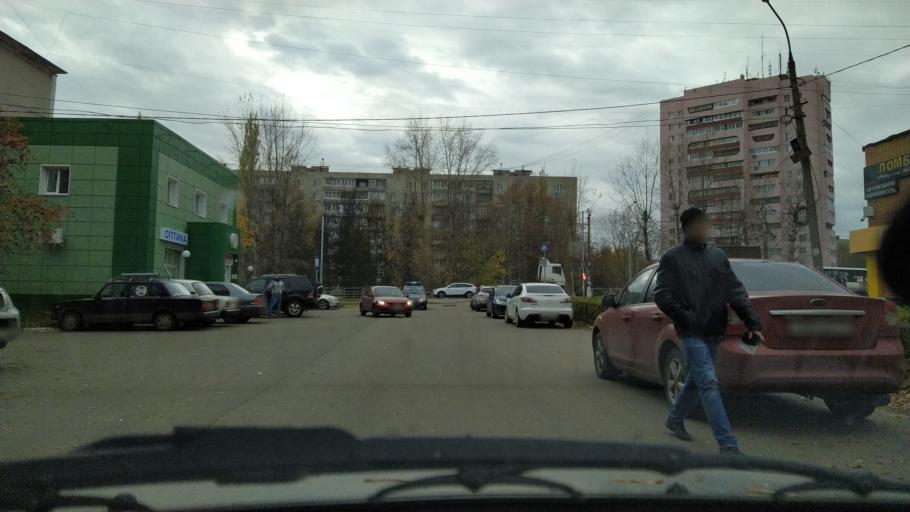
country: RU
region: Moskovskaya
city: Voskresensk
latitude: 55.3154
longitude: 38.6521
